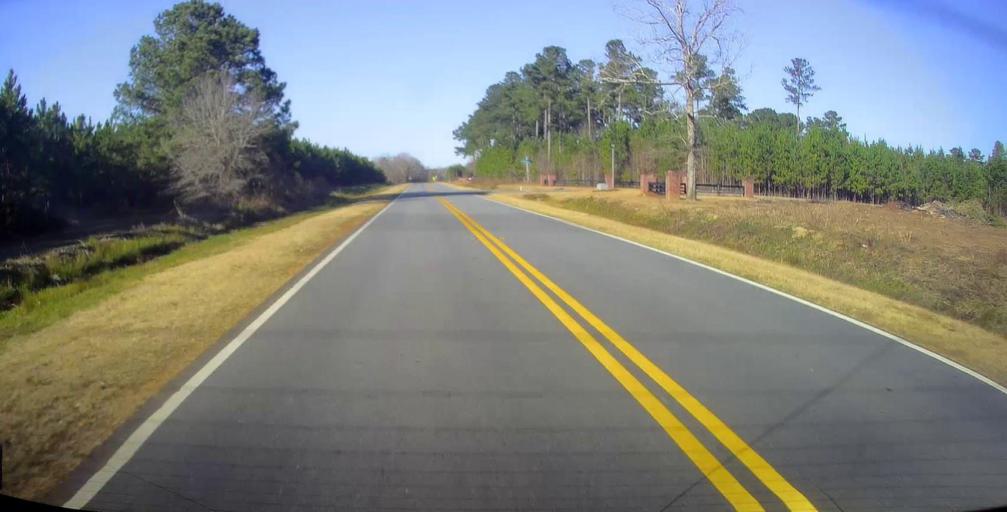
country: US
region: Georgia
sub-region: Sumter County
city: Americus
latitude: 32.1114
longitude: -84.1661
